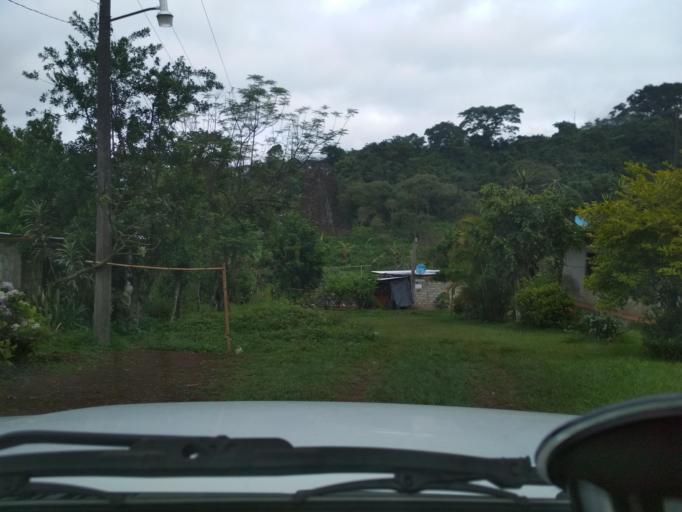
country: MX
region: Veracruz
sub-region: Fortin
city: Monte Salas
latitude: 18.9243
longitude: -97.0270
